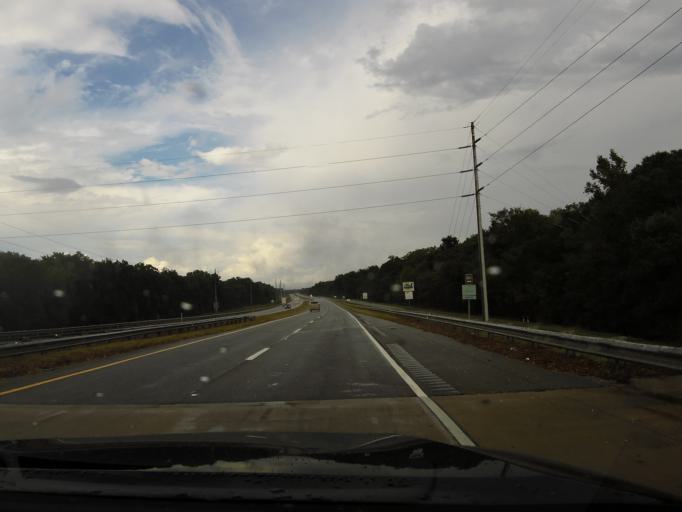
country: US
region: Georgia
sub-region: Wayne County
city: Jesup
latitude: 31.6681
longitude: -81.8352
